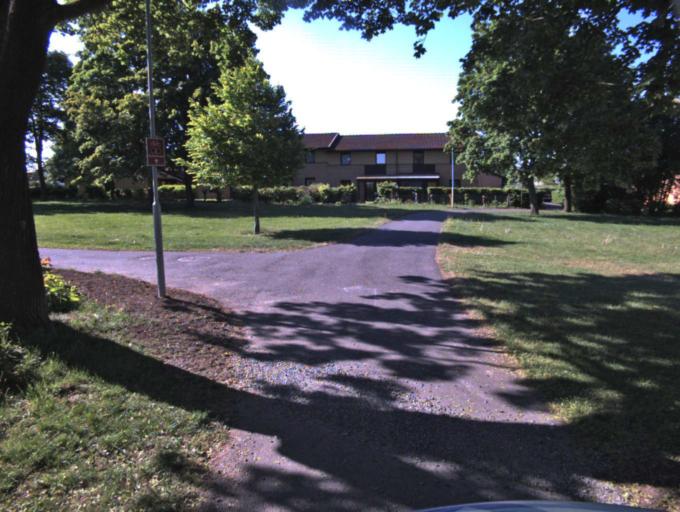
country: SE
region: Skane
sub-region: Kristianstads Kommun
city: Kristianstad
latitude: 56.0313
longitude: 14.2027
